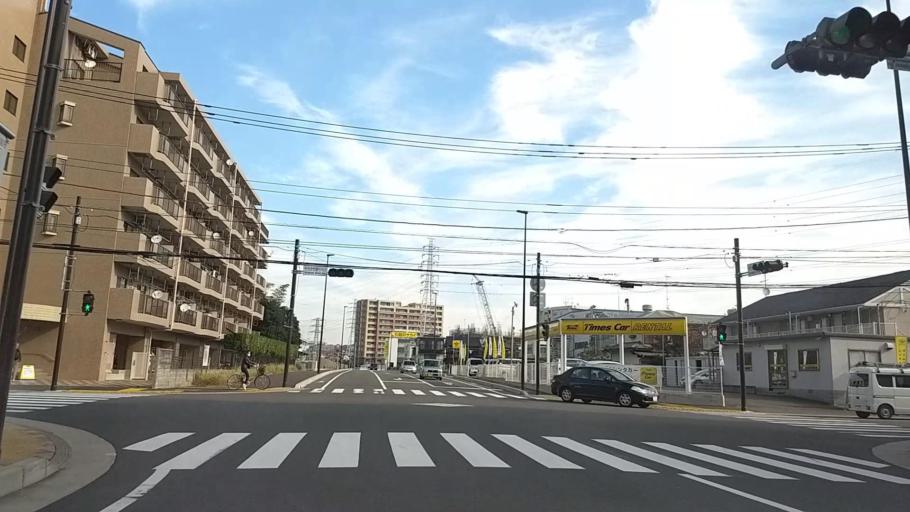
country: JP
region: Kanagawa
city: Zama
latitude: 35.4562
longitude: 139.3901
